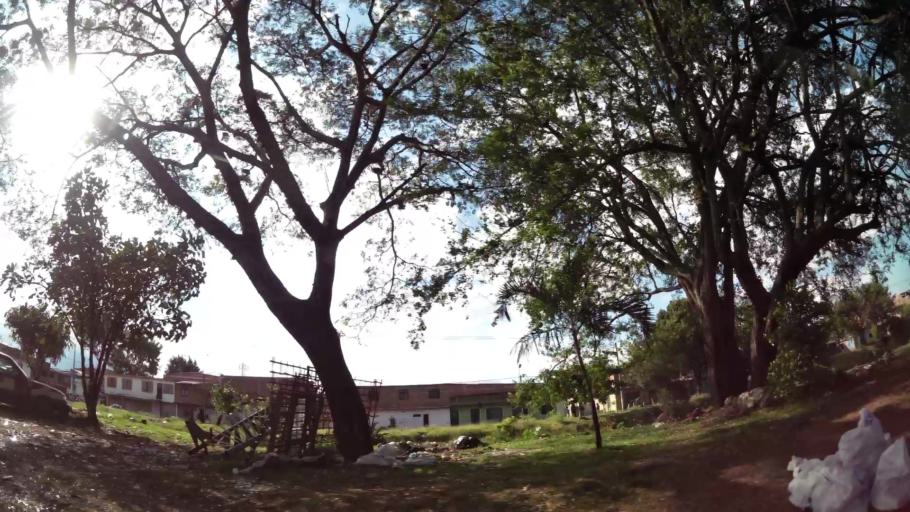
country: CO
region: Valle del Cauca
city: Cali
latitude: 3.4117
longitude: -76.5000
